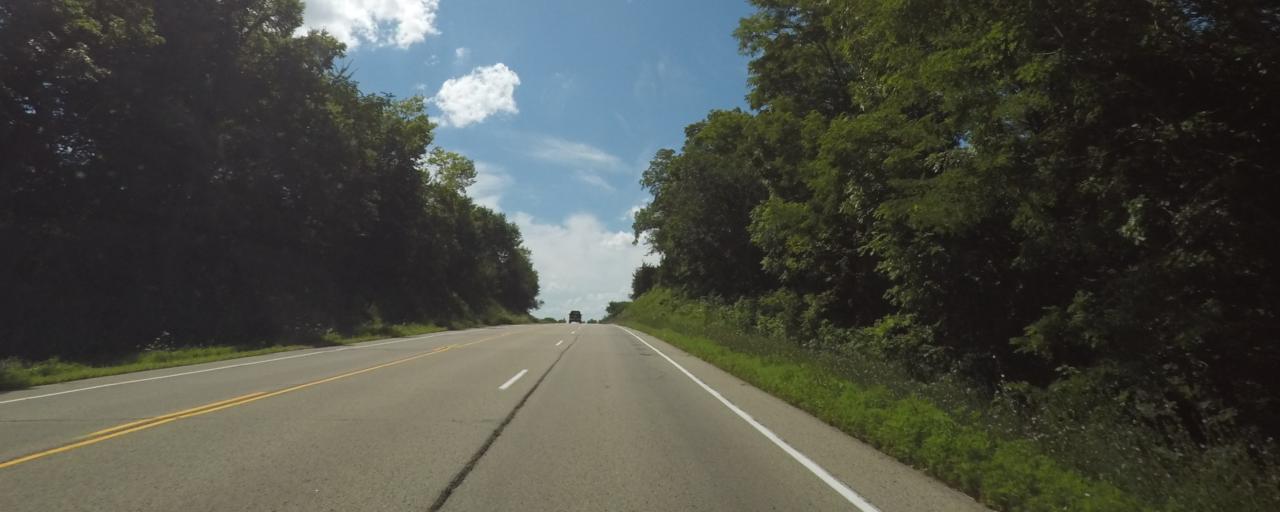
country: US
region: Wisconsin
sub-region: Dane County
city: Belleville
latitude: 42.8607
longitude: -89.5709
